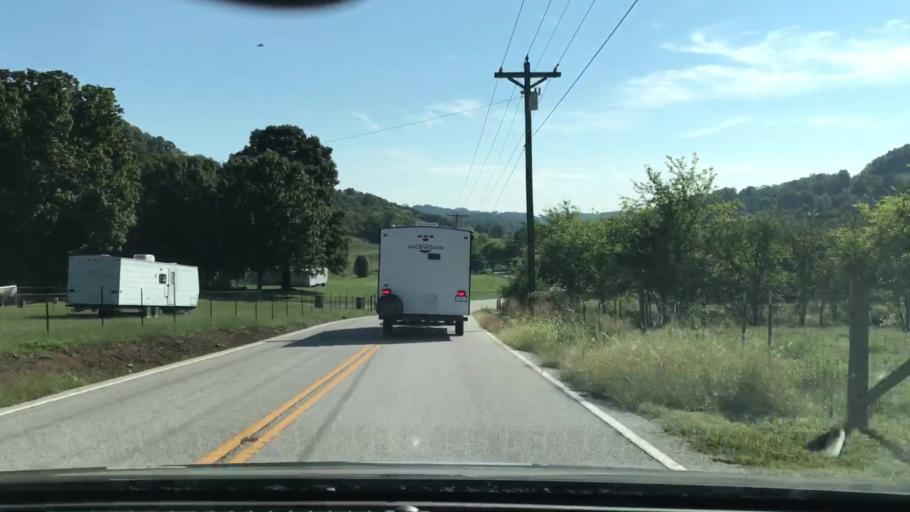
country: US
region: Tennessee
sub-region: Smith County
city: Carthage
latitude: 36.3484
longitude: -85.8435
